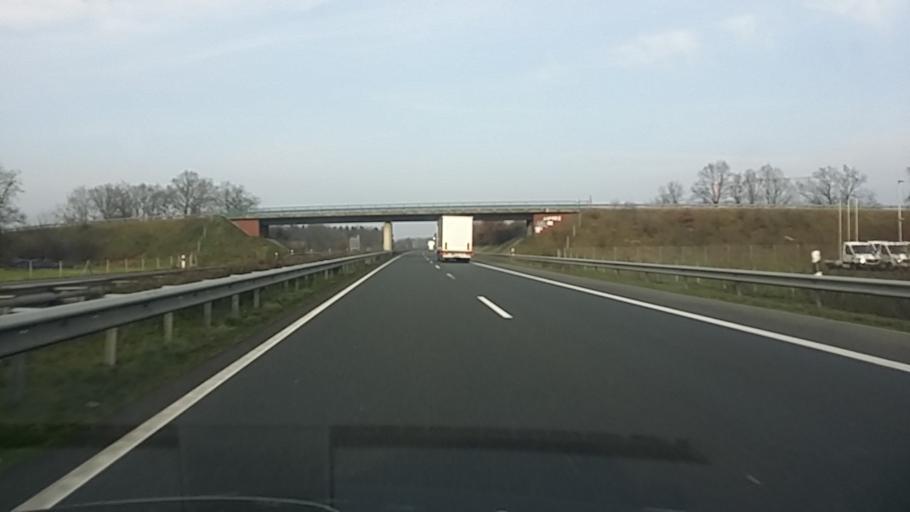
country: DE
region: Lower Saxony
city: Engden
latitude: 52.4834
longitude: 7.2102
